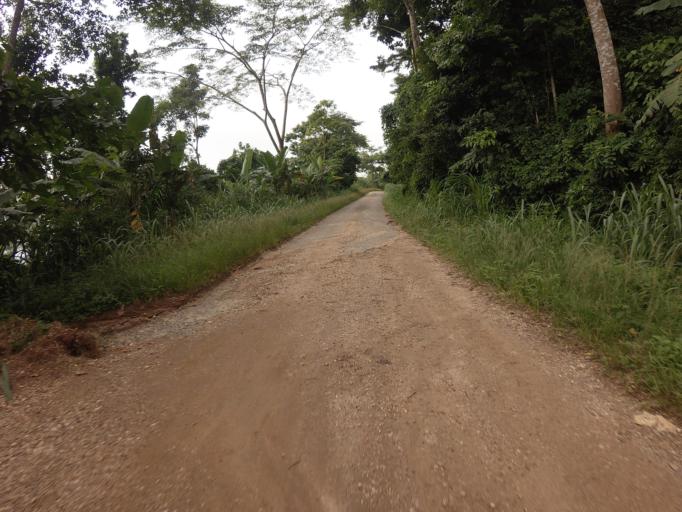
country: GH
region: Volta
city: Kpandu
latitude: 6.8376
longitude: 0.4277
